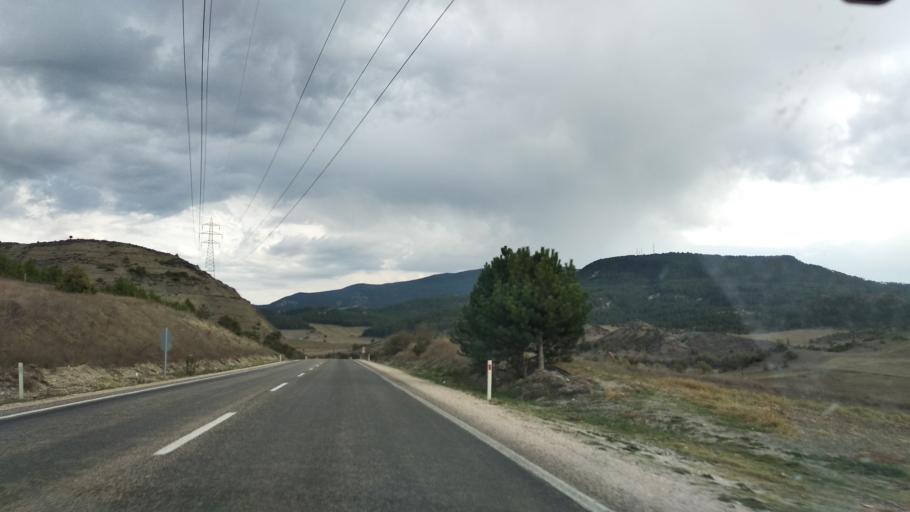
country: TR
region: Bolu
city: Mudurnu
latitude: 40.4786
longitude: 31.1652
